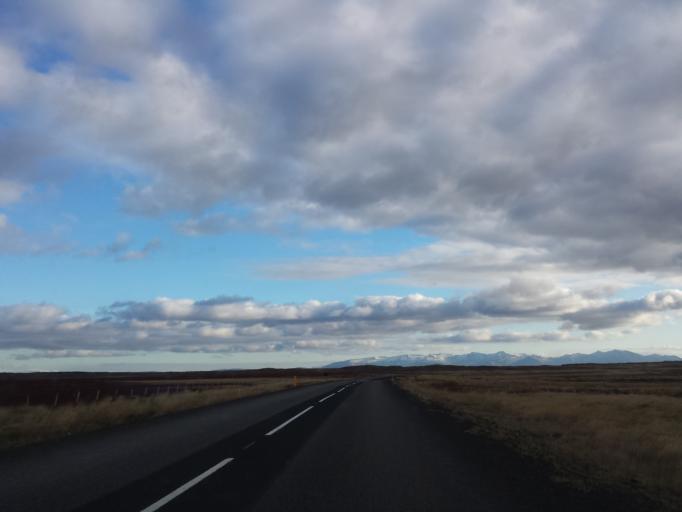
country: IS
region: West
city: Borgarnes
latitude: 64.7148
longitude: -22.1545
